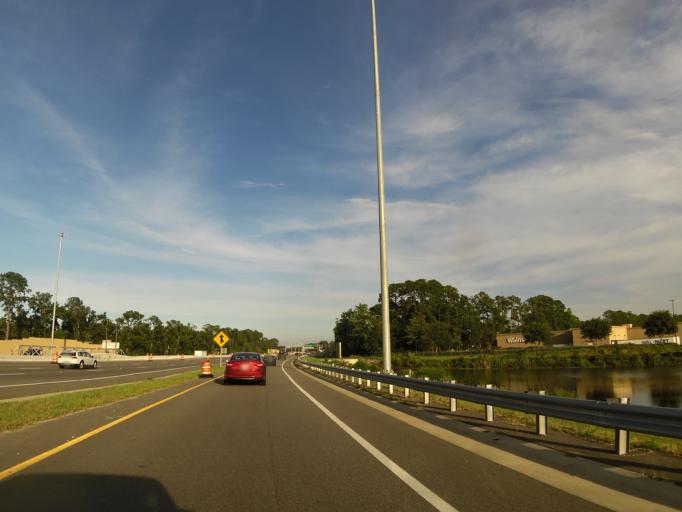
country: US
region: Florida
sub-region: Saint Johns County
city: Fruit Cove
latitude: 30.1797
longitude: -81.6258
